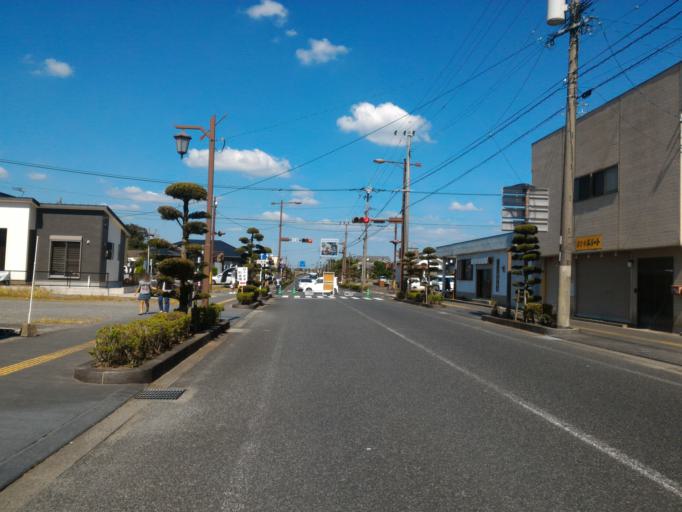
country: JP
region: Kagoshima
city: Kanoya
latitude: 31.3471
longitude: 130.9476
